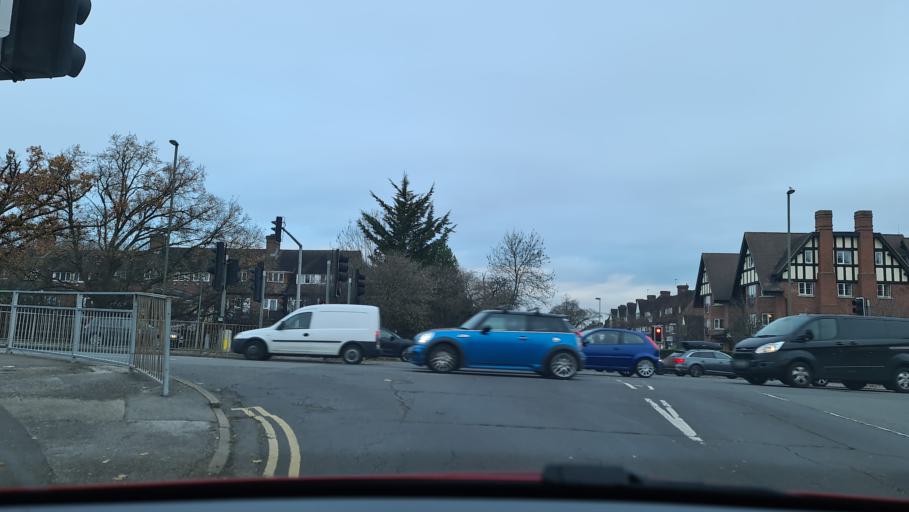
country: GB
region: England
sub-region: Surrey
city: Hinchley Wood
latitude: 51.3737
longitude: -0.3393
